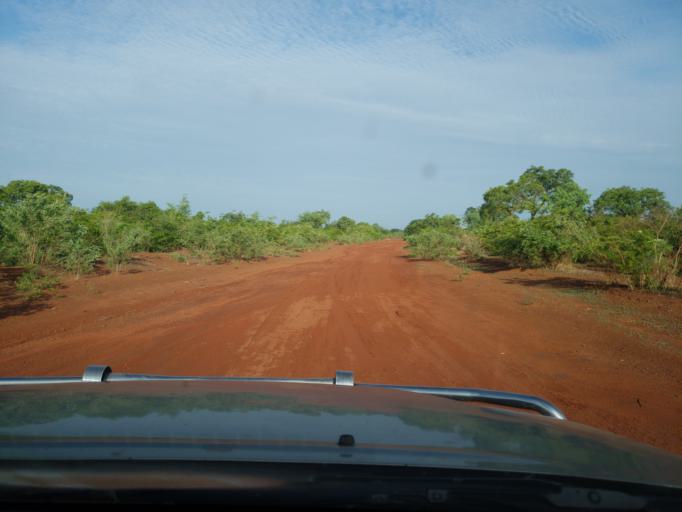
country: ML
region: Sikasso
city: Koutiala
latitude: 12.4255
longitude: -5.6500
